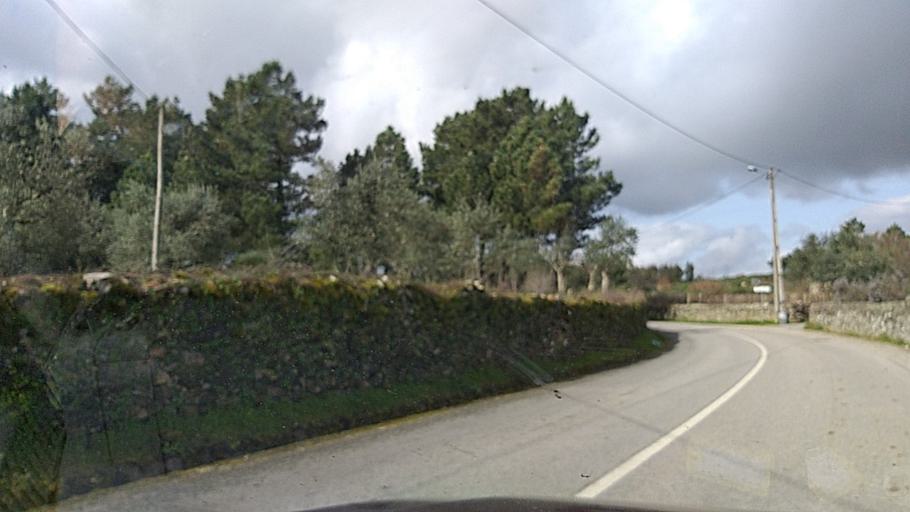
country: PT
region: Guarda
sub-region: Fornos de Algodres
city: Fornos de Algodres
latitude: 40.6627
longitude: -7.5707
